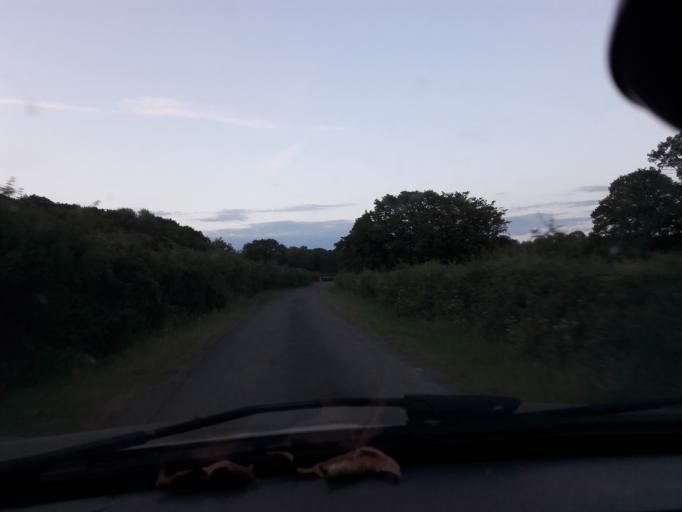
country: BE
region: Wallonia
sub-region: Province du Hainaut
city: Beaumont
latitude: 50.2681
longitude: 4.1927
